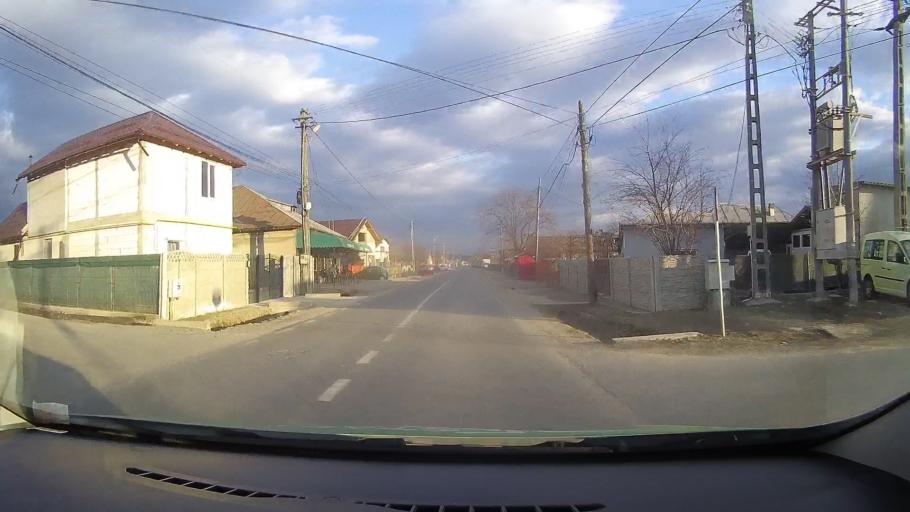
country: RO
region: Dambovita
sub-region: Comuna I. L. Caragiale
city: Ghirdoveni
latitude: 44.9445
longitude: 25.6649
